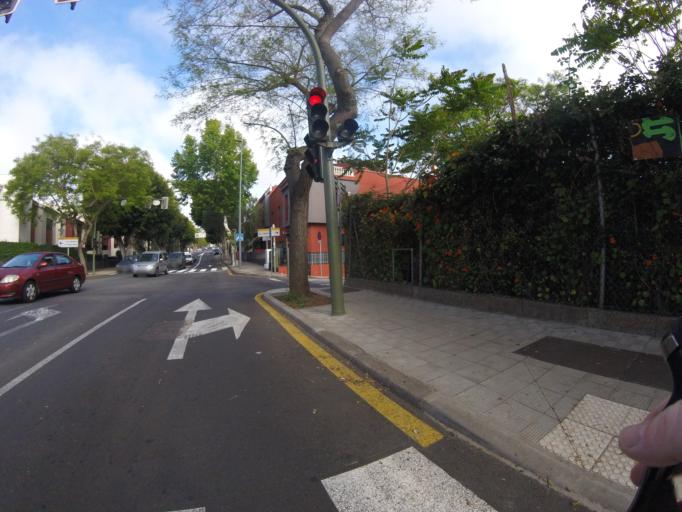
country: ES
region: Canary Islands
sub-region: Provincia de Santa Cruz de Tenerife
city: La Laguna
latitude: 28.4815
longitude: -16.3229
